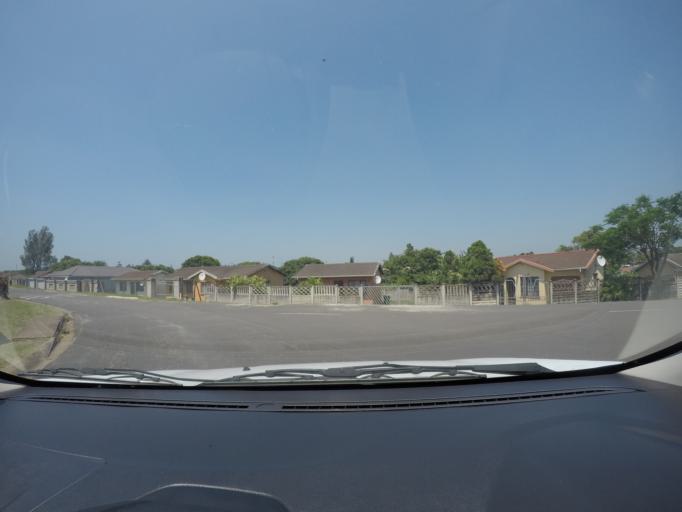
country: ZA
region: KwaZulu-Natal
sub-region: uThungulu District Municipality
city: eSikhawini
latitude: -28.8696
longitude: 31.9201
